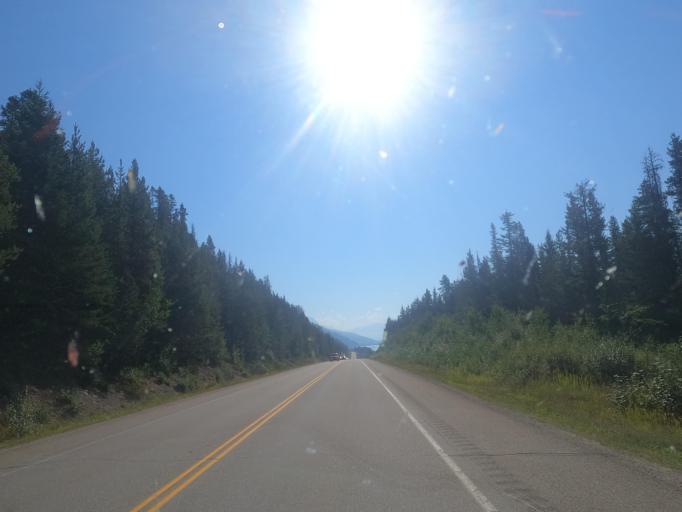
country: CA
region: Alberta
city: Jasper Park Lodge
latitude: 52.9628
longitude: -118.9131
